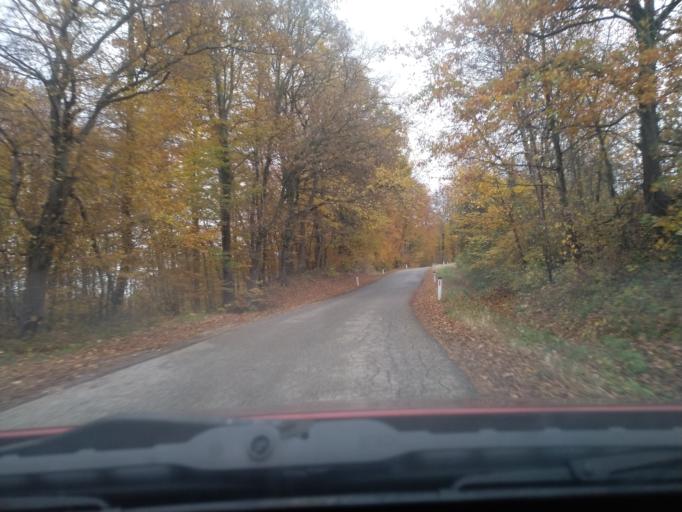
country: SI
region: Kungota
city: Zgornja Kungota
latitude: 46.6776
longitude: 15.6093
